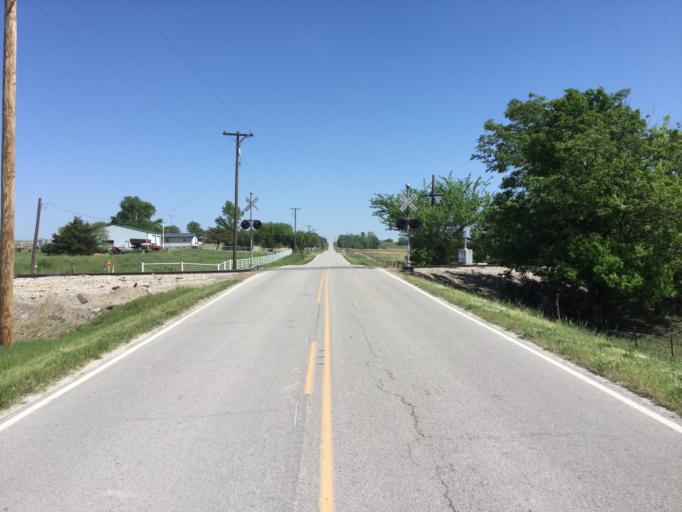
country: US
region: Kansas
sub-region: Montgomery County
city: Independence
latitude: 37.2515
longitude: -95.6567
